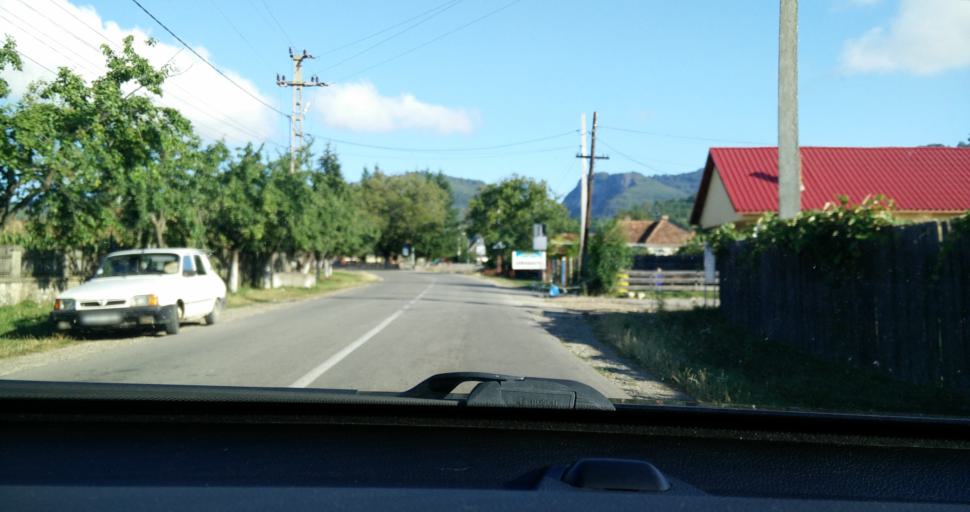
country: RO
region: Gorj
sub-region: Comuna Polovragi
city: Polovragi
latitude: 45.1761
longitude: 23.7991
